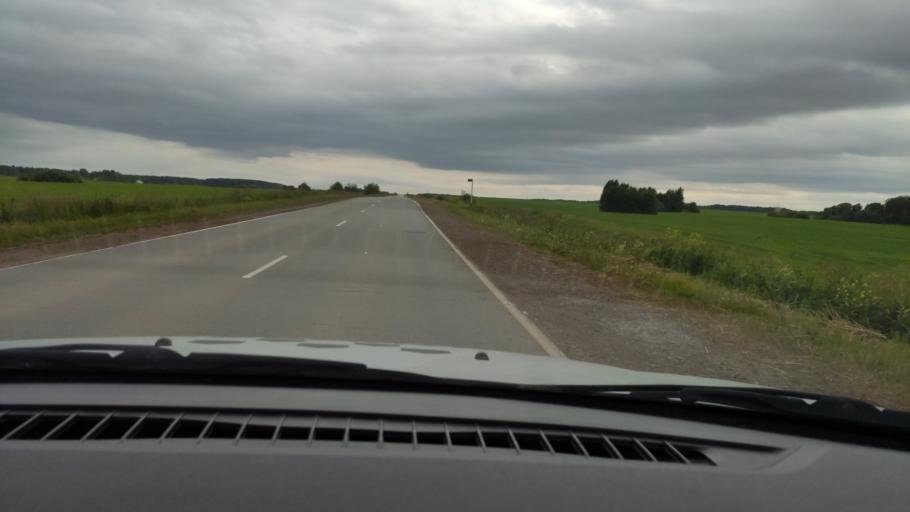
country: RU
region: Perm
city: Kungur
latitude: 57.3937
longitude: 56.8717
